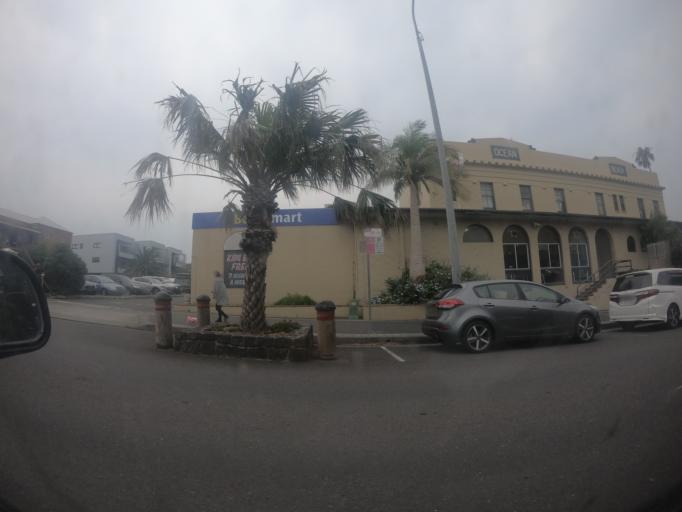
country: AU
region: New South Wales
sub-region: Shellharbour
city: Shellharbour Village
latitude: -34.5785
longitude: 150.8696
